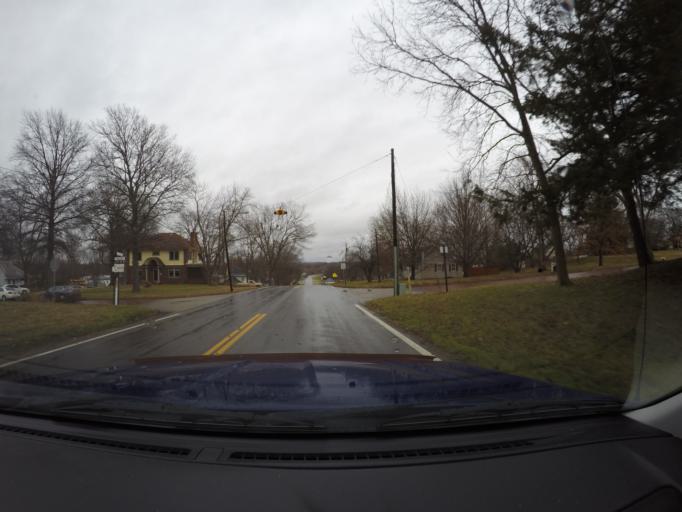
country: US
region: Kansas
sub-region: Jefferson County
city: Valley Falls
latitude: 39.3409
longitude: -95.4630
